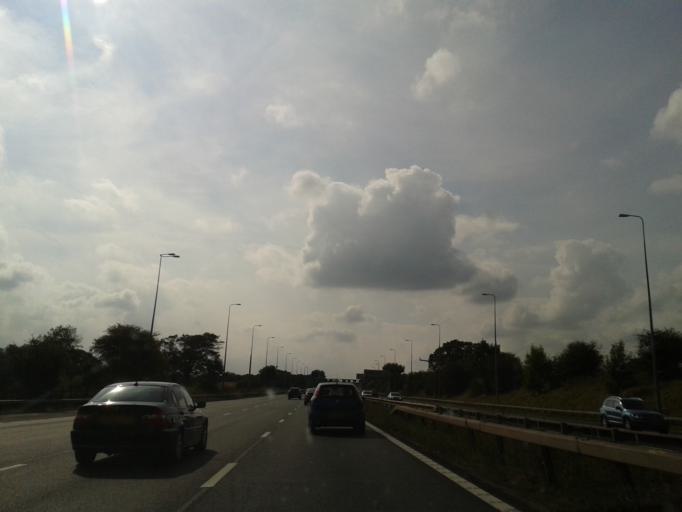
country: GB
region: England
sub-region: Solihull
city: Bickenhill
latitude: 52.4212
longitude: -1.7217
